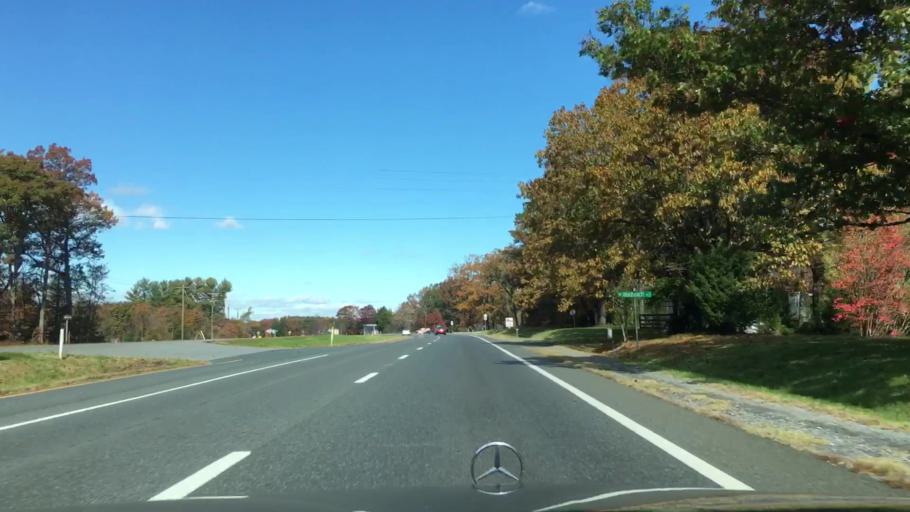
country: US
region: Virginia
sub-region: Campbell County
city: Rustburg
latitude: 37.2340
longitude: -79.1856
